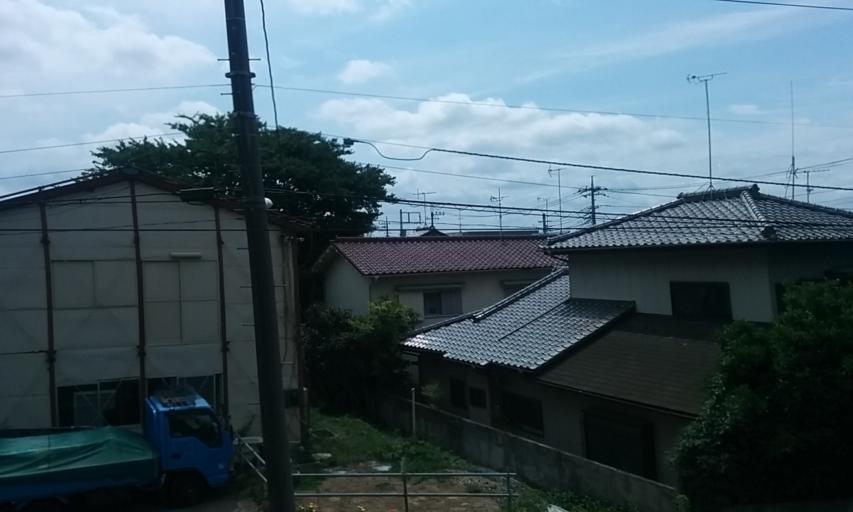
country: JP
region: Chiba
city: Yotsukaido
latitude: 35.6961
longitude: 140.0847
